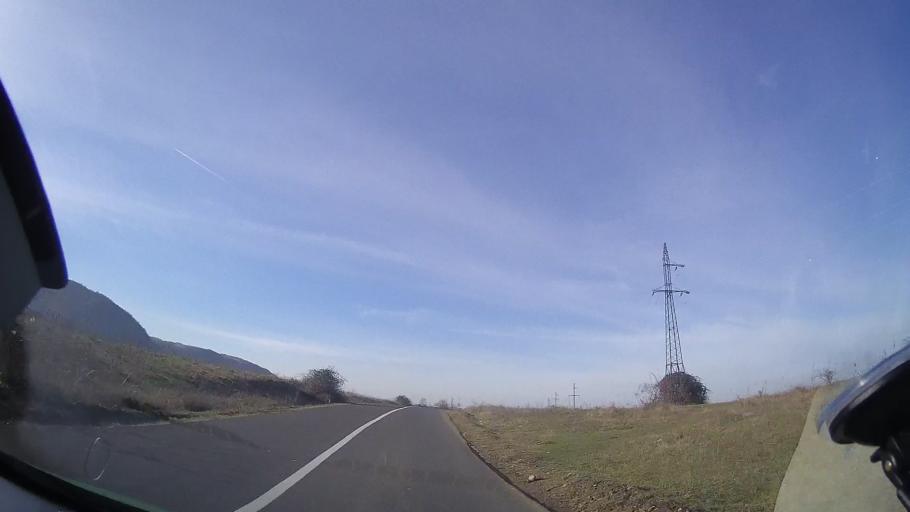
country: RO
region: Bihor
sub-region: Comuna Astileu
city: Astileu
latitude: 47.0243
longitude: 22.4080
